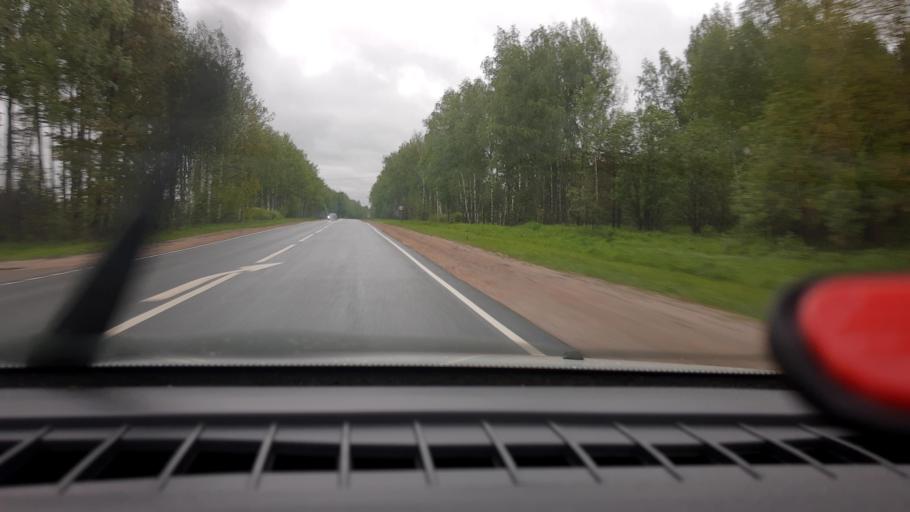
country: RU
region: Nizjnij Novgorod
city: Krasnyye Baki
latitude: 57.0538
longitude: 45.1364
